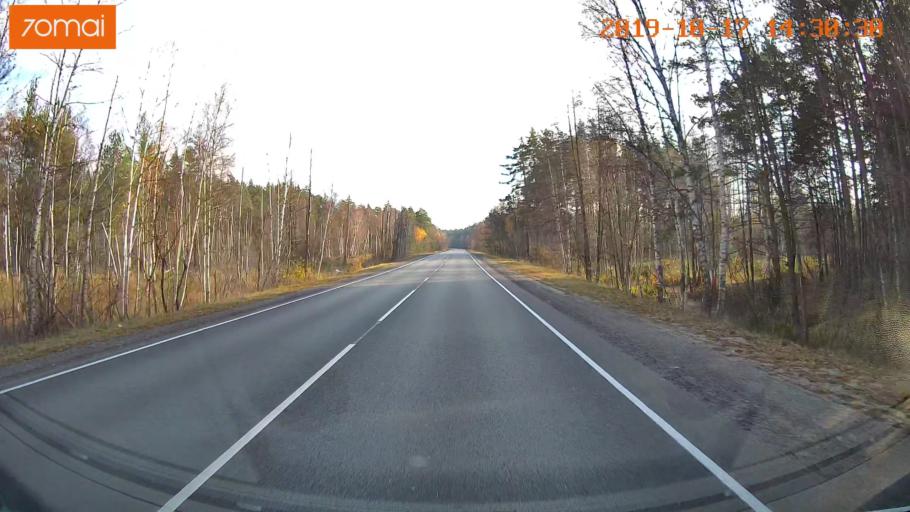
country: RU
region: Rjazan
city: Solotcha
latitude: 54.9468
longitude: 39.9470
